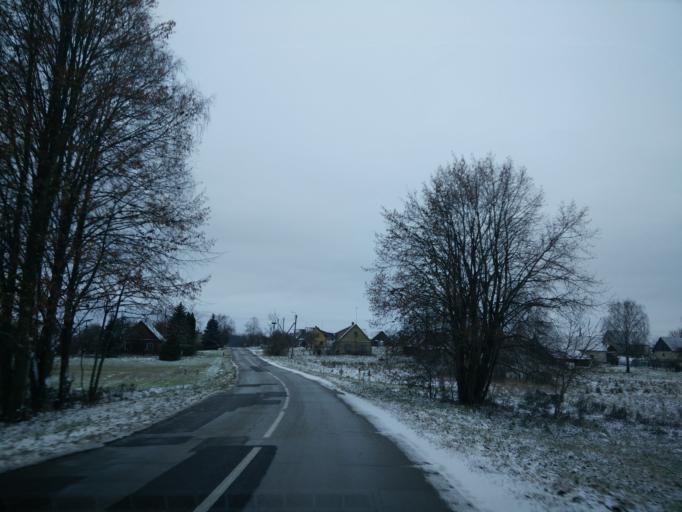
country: LT
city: Tytuveneliai
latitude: 55.4939
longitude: 23.3332
